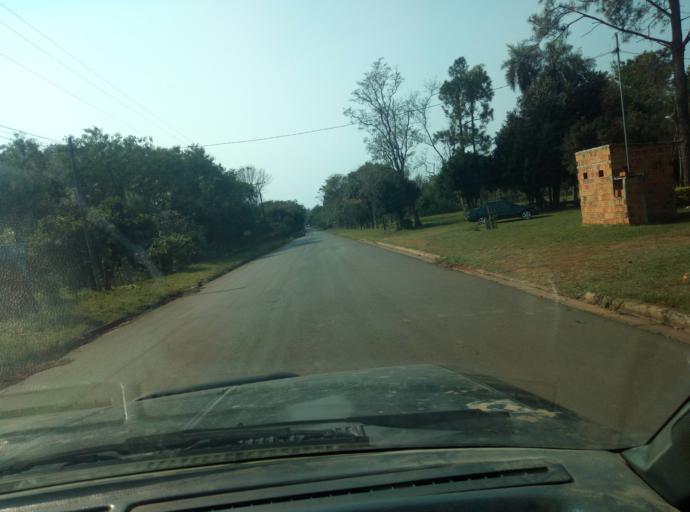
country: PY
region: Caaguazu
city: Carayao
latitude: -25.2102
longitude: -56.3041
